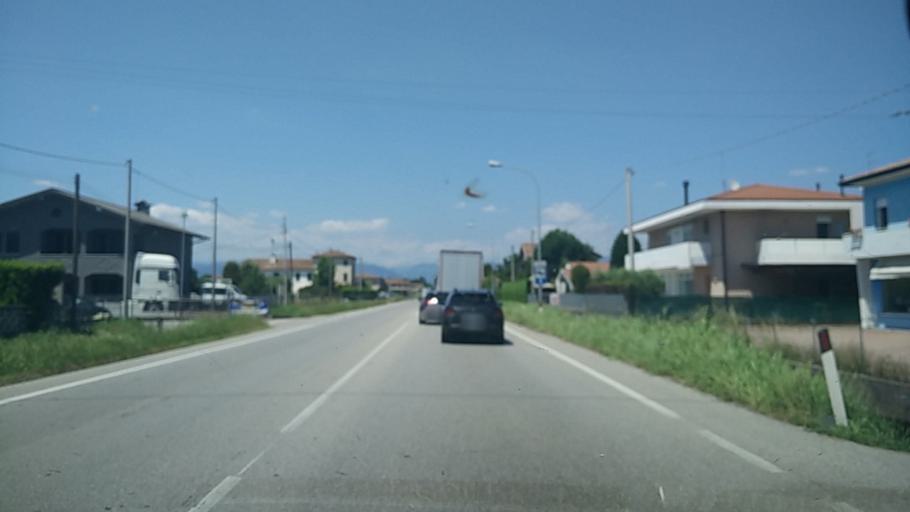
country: IT
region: Veneto
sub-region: Provincia di Padova
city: San Giorgio in Bosco
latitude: 45.6138
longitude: 11.7974
